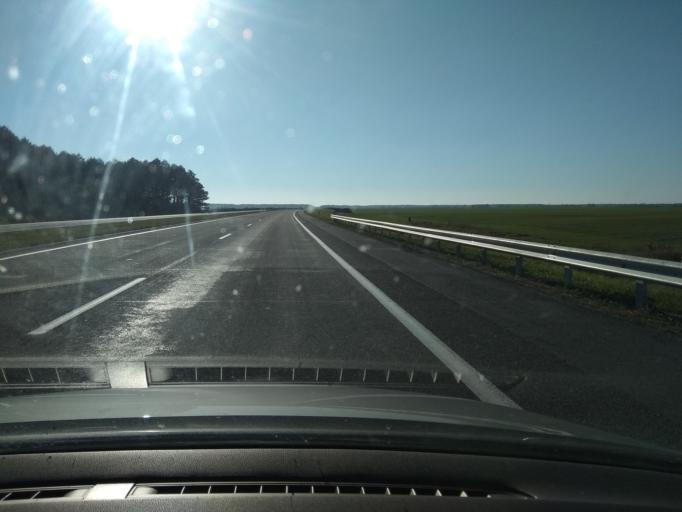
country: BY
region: Brest
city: Ivatsevichy
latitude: 52.6759
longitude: 25.3190
